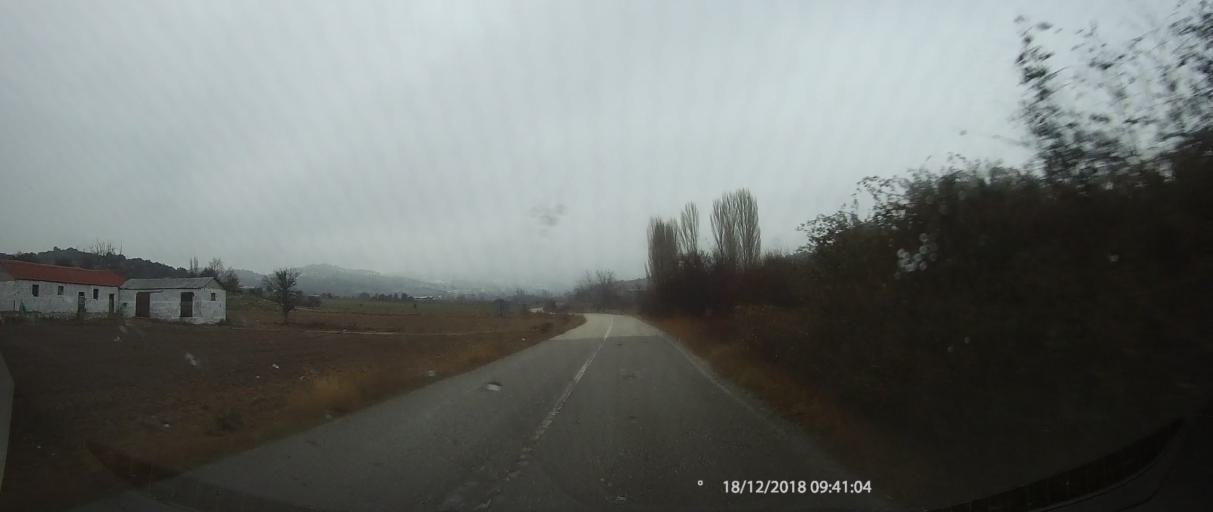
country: GR
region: Thessaly
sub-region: Nomos Larisis
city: Elassona
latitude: 40.0082
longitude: 22.2306
